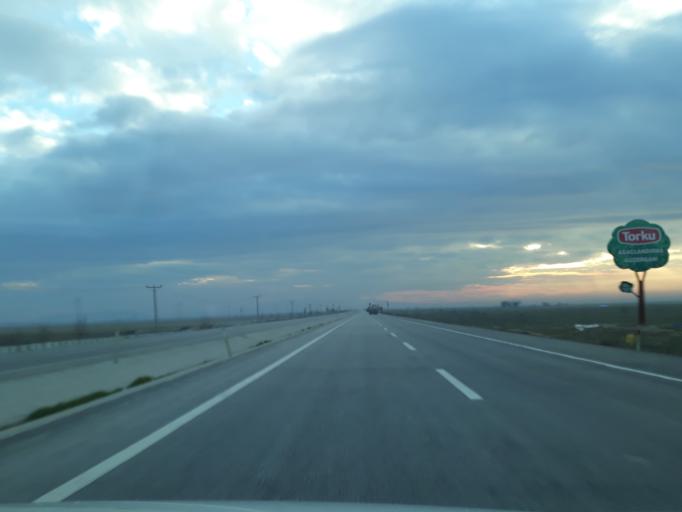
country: TR
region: Konya
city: Hotamis
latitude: 37.7108
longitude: 33.2856
